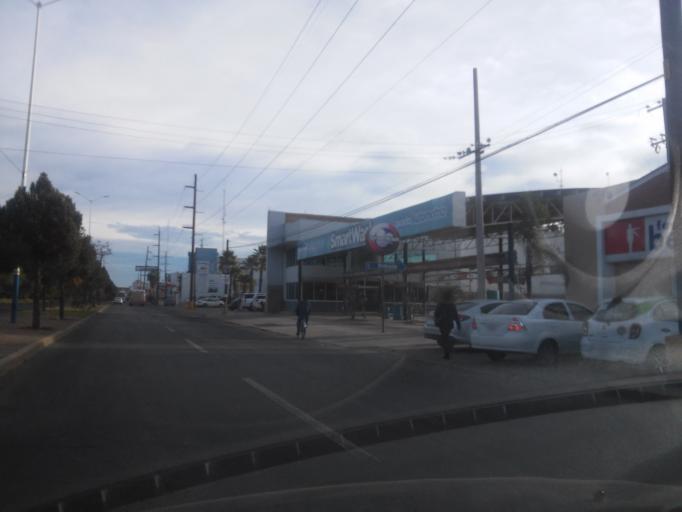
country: MX
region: Durango
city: Victoria de Durango
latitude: 24.0374
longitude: -104.6340
